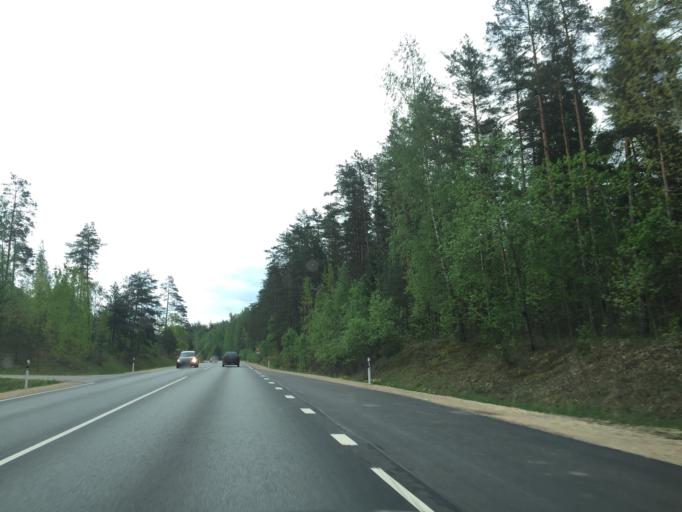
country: LV
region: Ikskile
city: Ikskile
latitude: 56.8935
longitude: 24.4470
